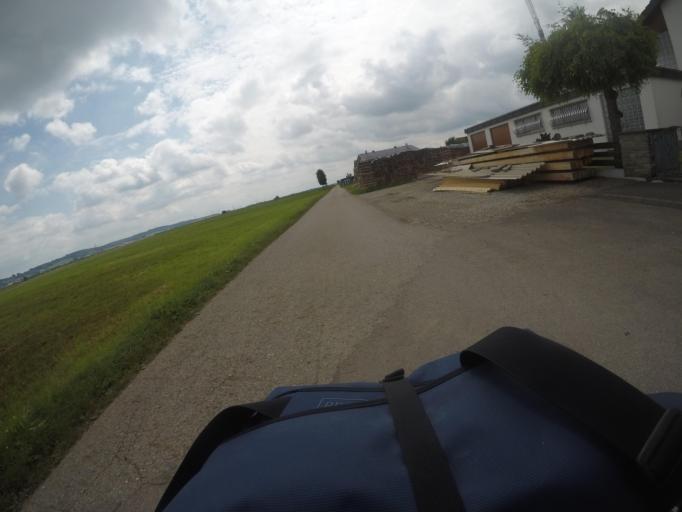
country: DE
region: Bavaria
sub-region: Swabia
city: Fellheim
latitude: 48.0696
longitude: 10.1564
